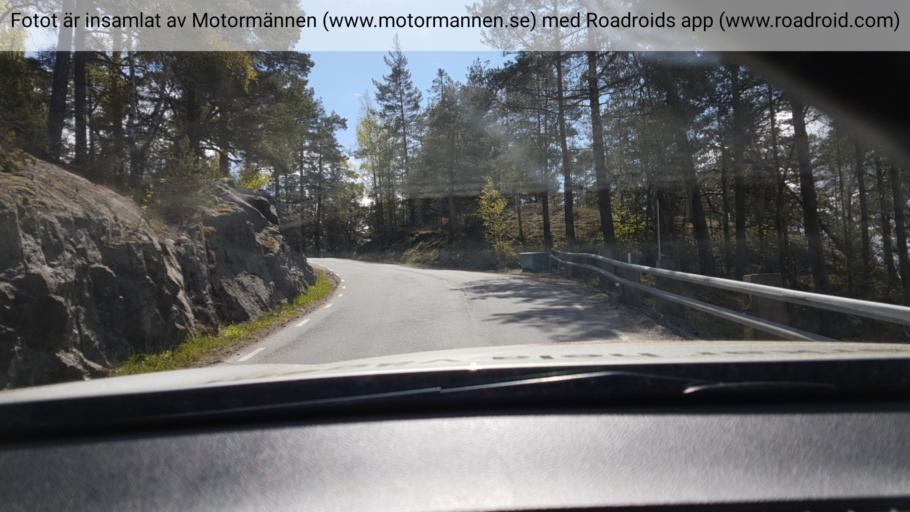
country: SE
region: Stockholm
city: Dalaro
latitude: 59.1513
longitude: 18.4335
